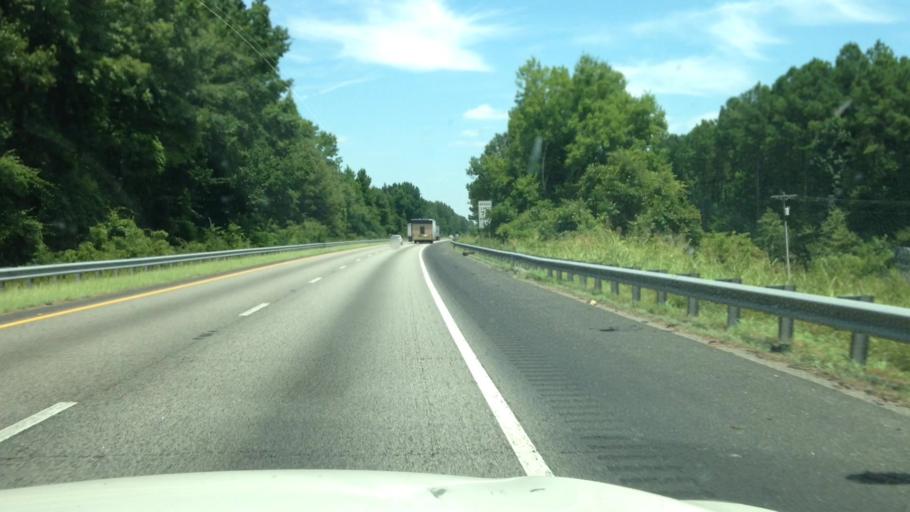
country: US
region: South Carolina
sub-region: Florence County
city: Florence
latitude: 34.2835
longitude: -79.6769
